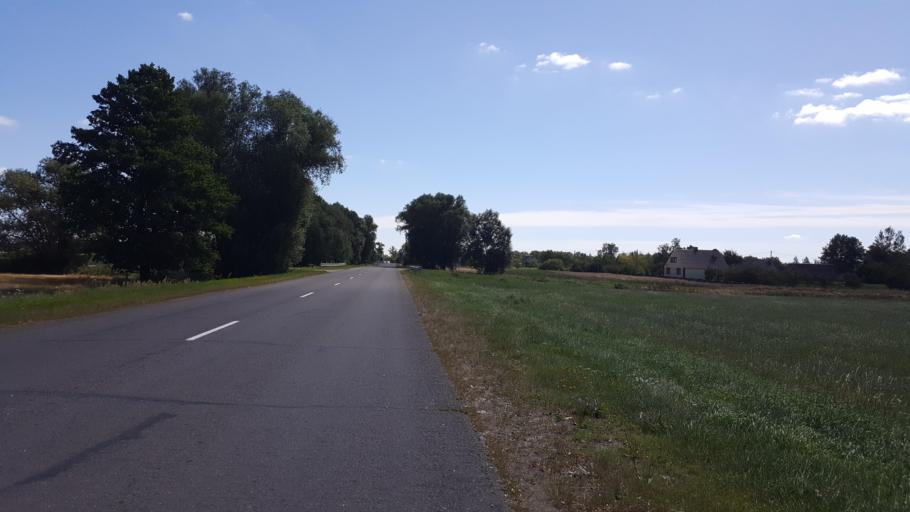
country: BY
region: Brest
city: Kobryn
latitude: 52.3432
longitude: 24.2255
